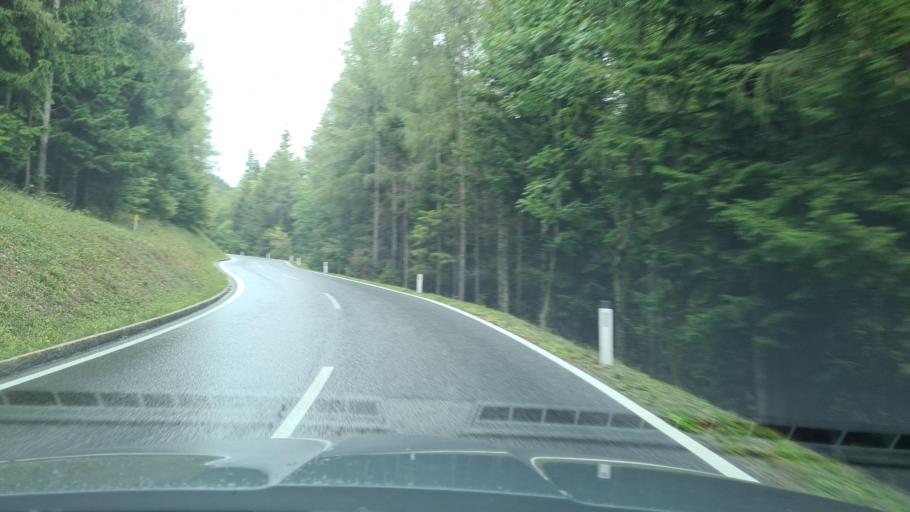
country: AT
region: Styria
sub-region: Politischer Bezirk Weiz
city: Passail
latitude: 47.3027
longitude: 15.4875
